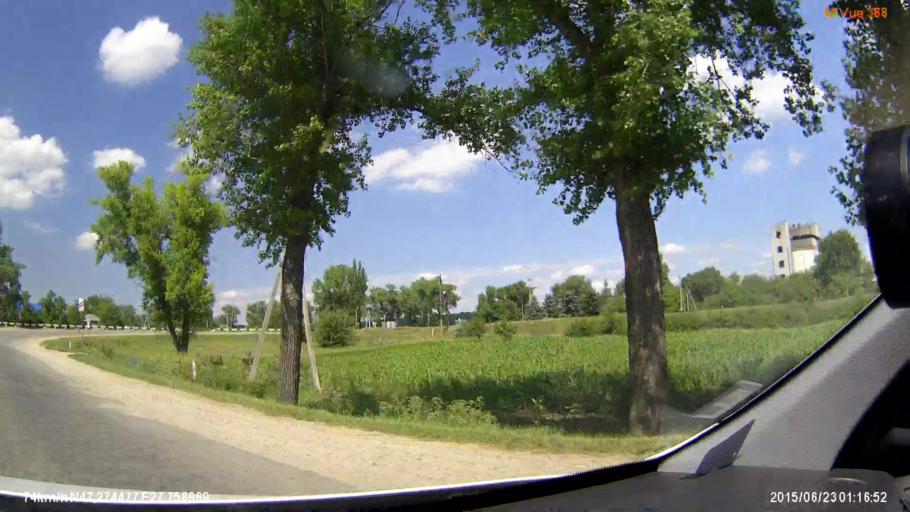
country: RO
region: Iasi
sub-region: Comuna Ungheni
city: Bosia
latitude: 47.2743
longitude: 27.7590
